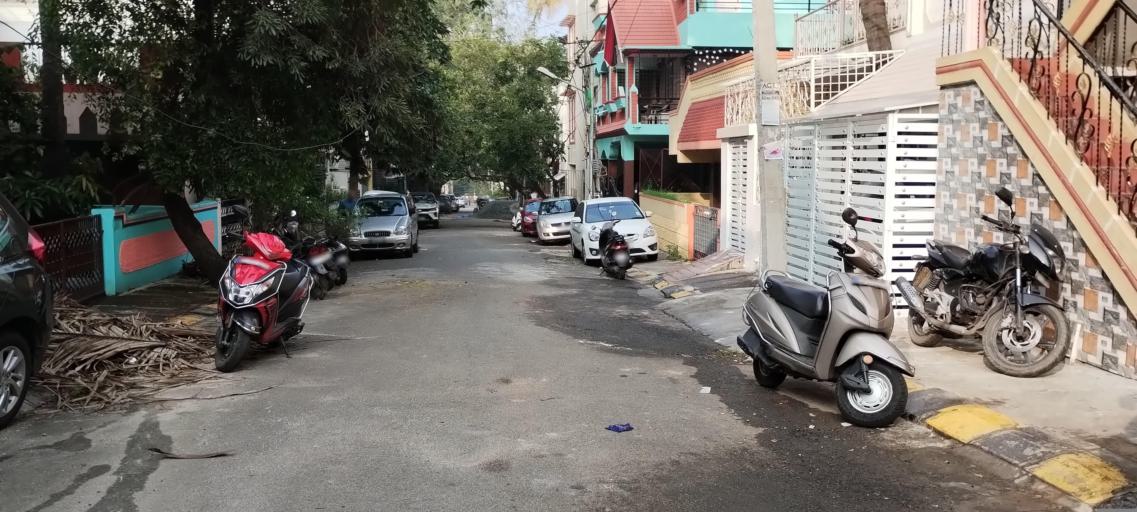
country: IN
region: Karnataka
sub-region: Bangalore Urban
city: Bangalore
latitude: 12.9403
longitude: 77.5448
